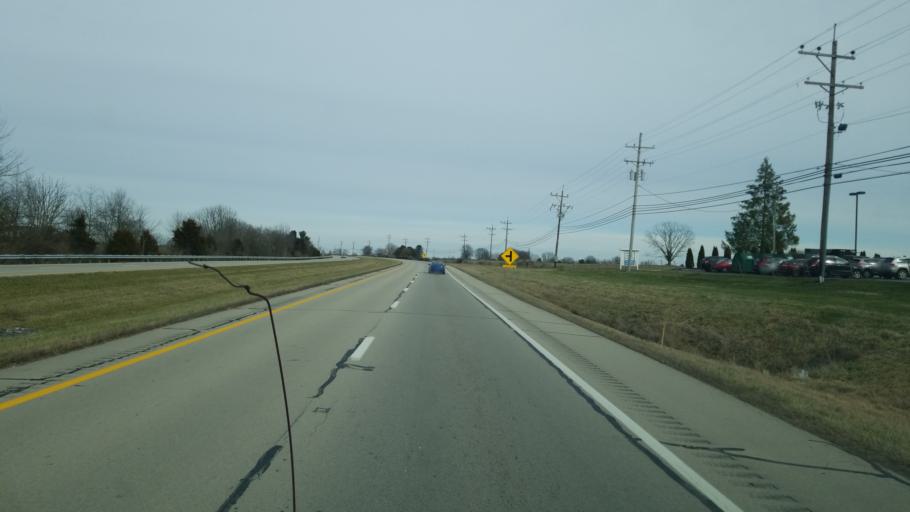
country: US
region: Ohio
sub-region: Brown County
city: Ripley
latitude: 38.7814
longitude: -83.8084
